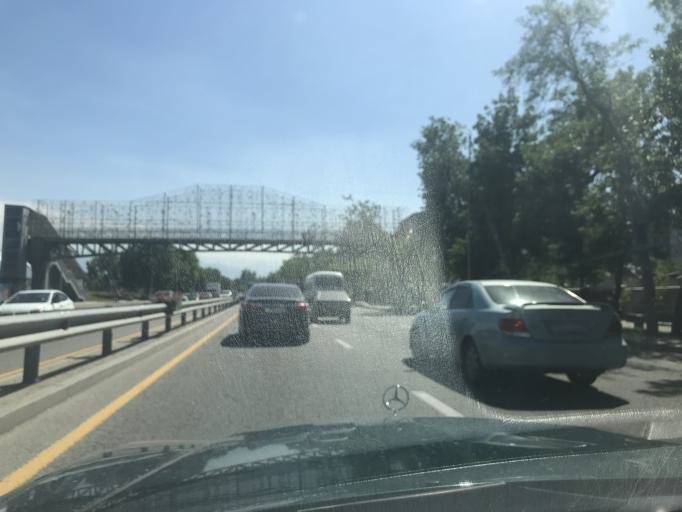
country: KZ
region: Almaty Qalasy
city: Almaty
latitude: 43.2901
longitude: 76.9903
